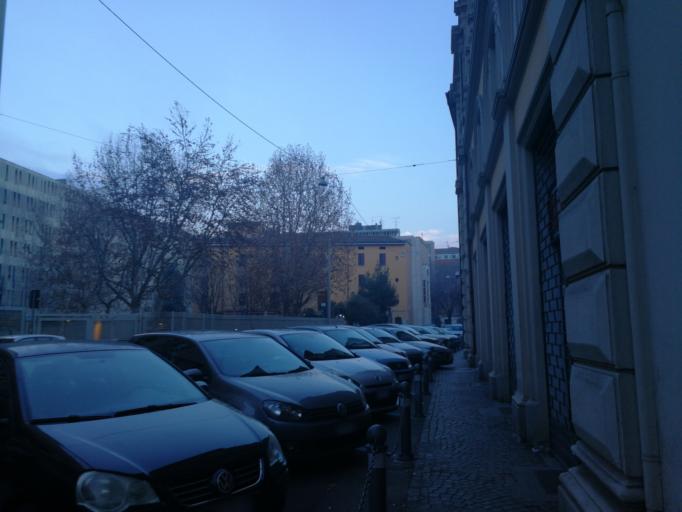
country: IT
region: Emilia-Romagna
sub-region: Provincia di Bologna
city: Bologna
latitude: 44.5014
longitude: 11.3397
